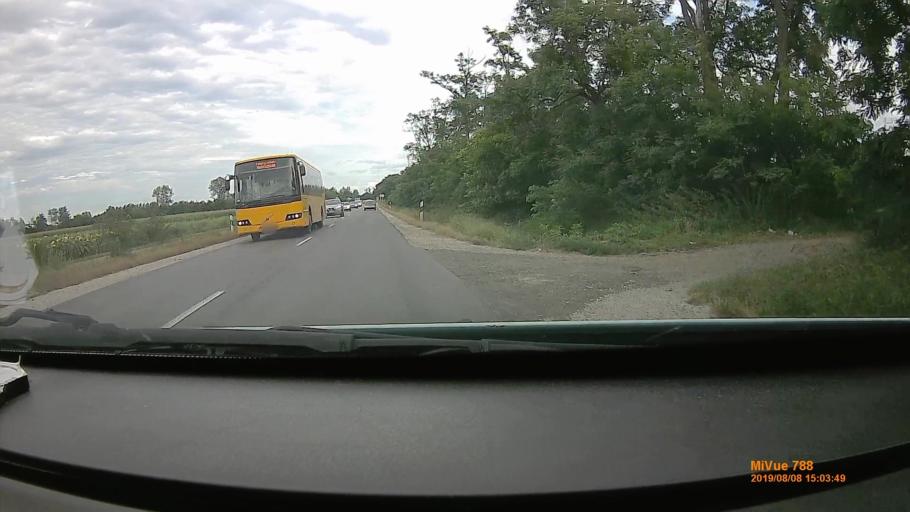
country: HU
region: Szabolcs-Szatmar-Bereg
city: Kocsord
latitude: 47.9373
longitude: 22.4180
